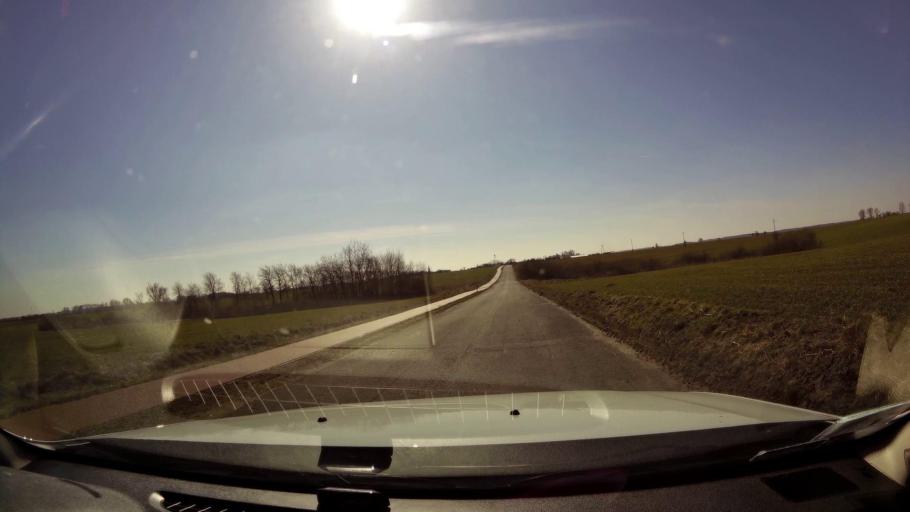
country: PL
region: West Pomeranian Voivodeship
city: Trzcinsko Zdroj
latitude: 52.9813
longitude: 14.6074
